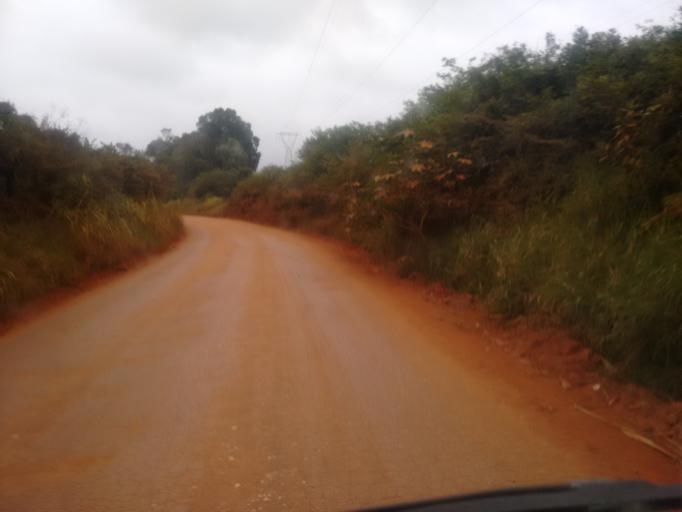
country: BR
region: Rio Grande do Sul
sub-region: Camaqua
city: Camaqua
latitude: -30.8262
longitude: -51.8151
